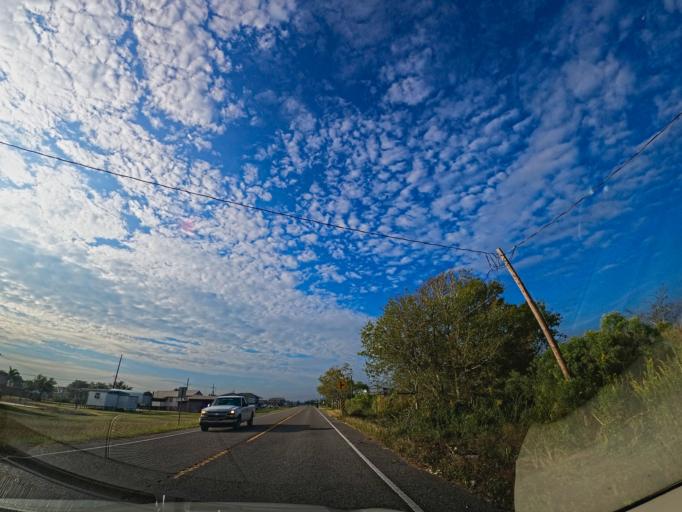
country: US
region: Louisiana
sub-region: Terrebonne Parish
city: Dulac
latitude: 29.3094
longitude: -90.6478
